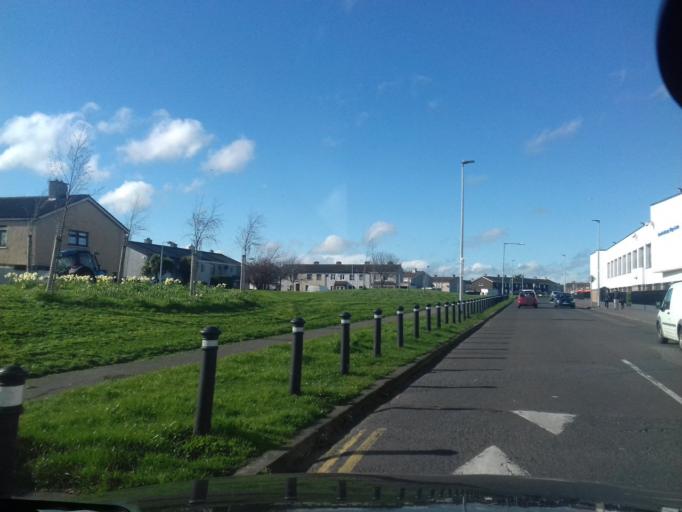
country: IE
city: Darndale
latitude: 53.4011
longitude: -6.1949
